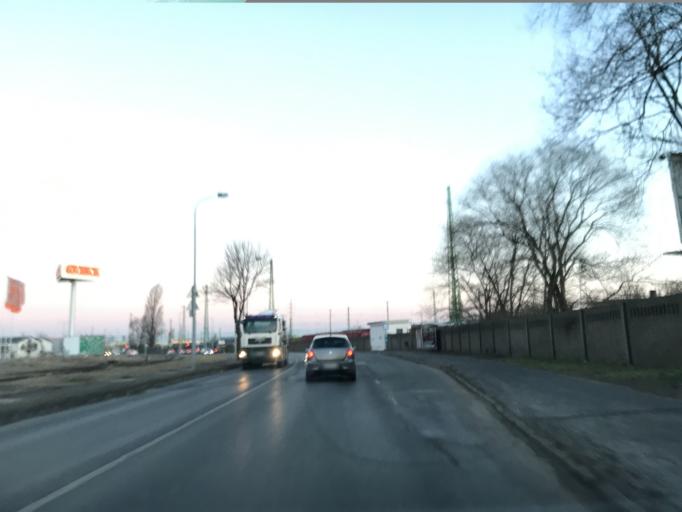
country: HU
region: Gyor-Moson-Sopron
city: Gyor
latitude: 47.6862
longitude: 17.6495
